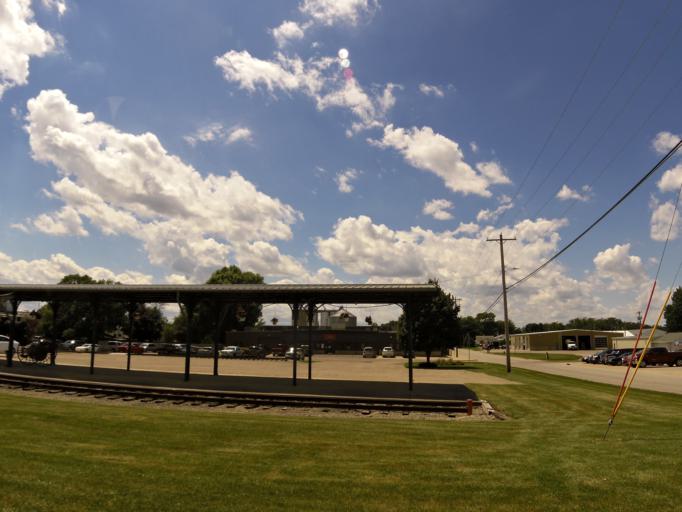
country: US
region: Iowa
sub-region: Buchanan County
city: Independence
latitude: 42.4791
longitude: -91.8895
